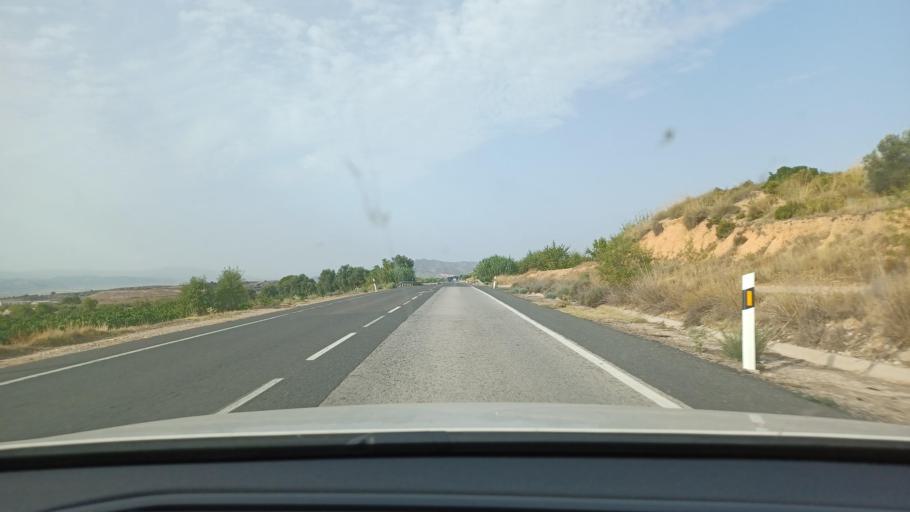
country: ES
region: Castille-La Mancha
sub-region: Provincia de Albacete
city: Caudete
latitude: 38.7393
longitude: -0.9309
